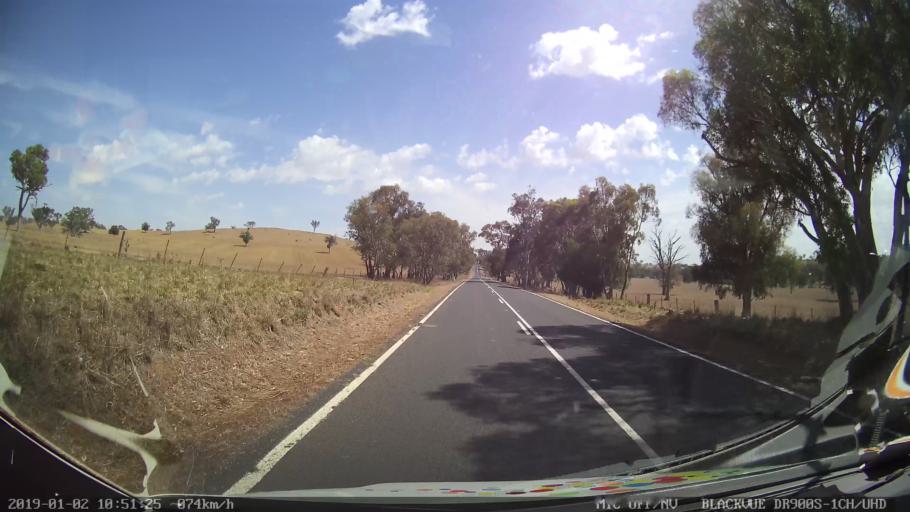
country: AU
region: New South Wales
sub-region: Cootamundra
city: Cootamundra
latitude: -34.7003
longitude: 148.2758
